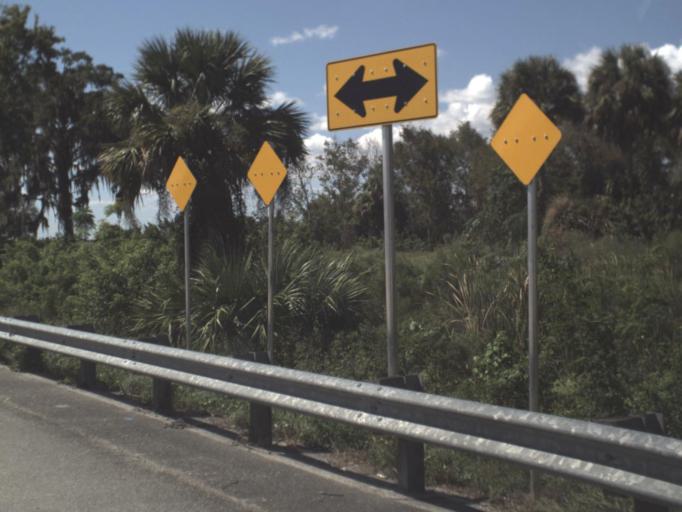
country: US
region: Florida
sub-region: Glades County
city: Buckhead Ridge
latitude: 27.1438
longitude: -80.8793
